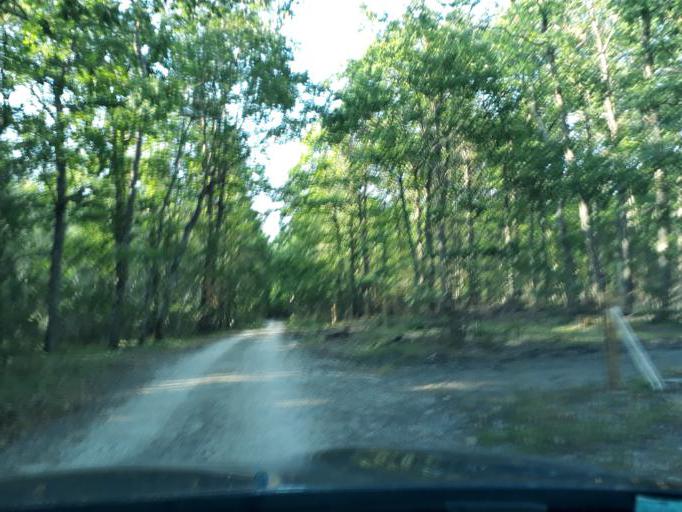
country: FR
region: Centre
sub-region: Departement du Loiret
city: Chaingy
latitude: 47.9092
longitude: 1.7417
